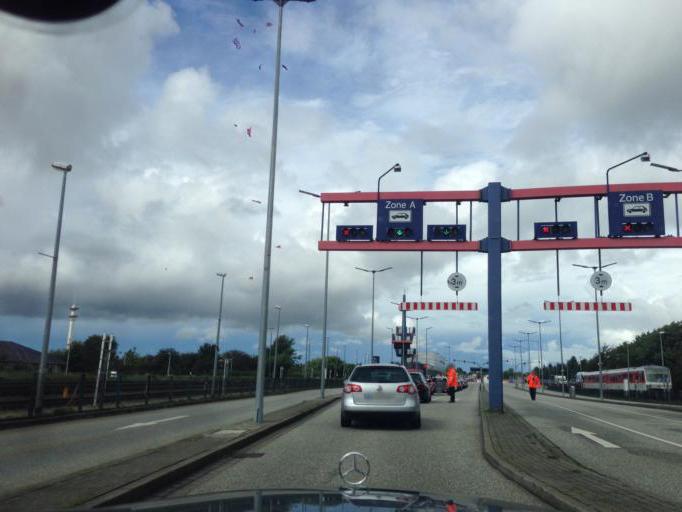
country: DE
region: Schleswig-Holstein
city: Niebull
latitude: 54.7827
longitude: 8.8378
